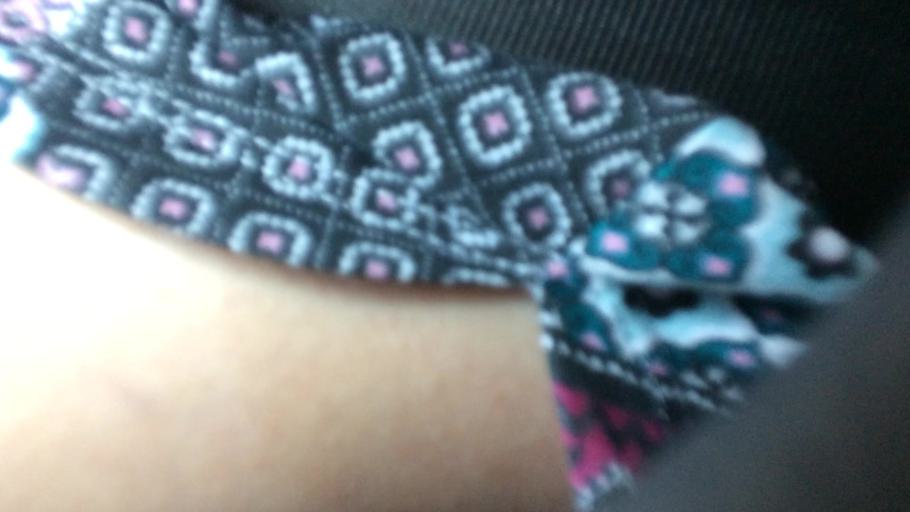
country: US
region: New Mexico
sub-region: Colfax County
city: Springer
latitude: 36.2108
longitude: -104.6619
